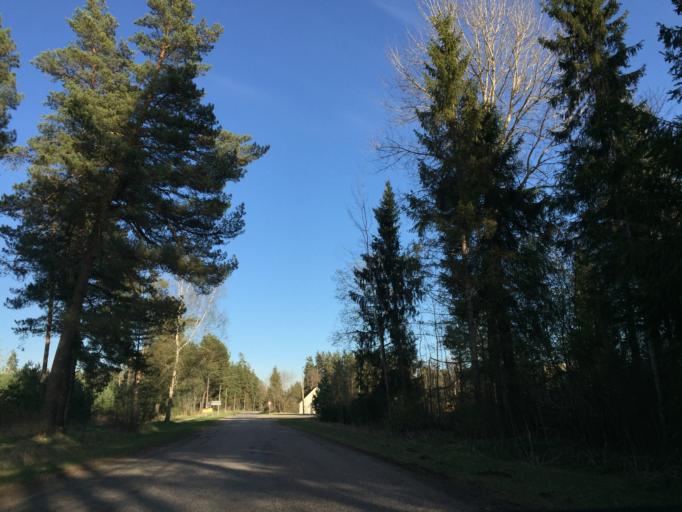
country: LV
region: Valkas Rajons
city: Valka
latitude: 57.7897
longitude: 25.9864
